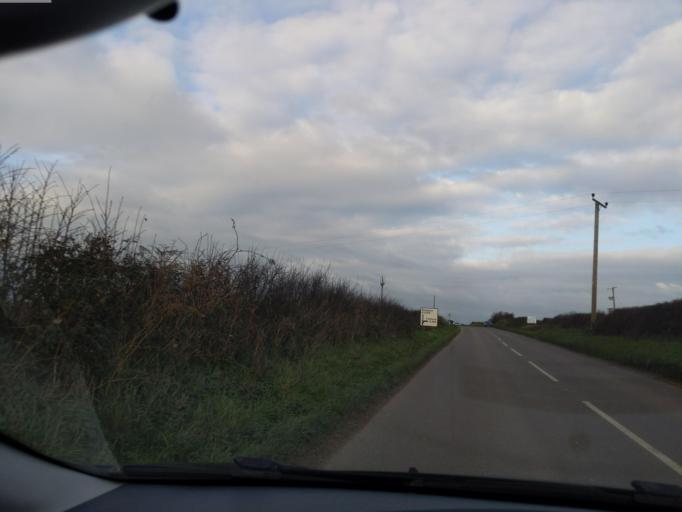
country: GB
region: England
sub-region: Cornwall
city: Padstow
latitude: 50.5317
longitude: -4.9516
